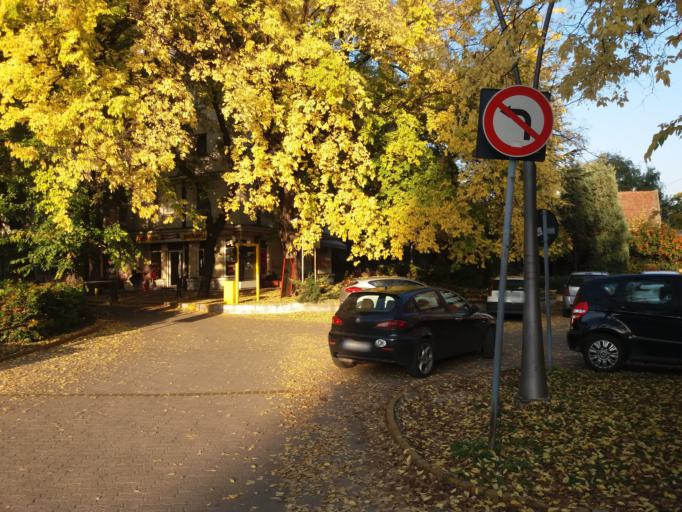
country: RS
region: Autonomna Pokrajina Vojvodina
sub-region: Severnobacki Okrug
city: Subotica
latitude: 46.1019
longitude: 19.6658
